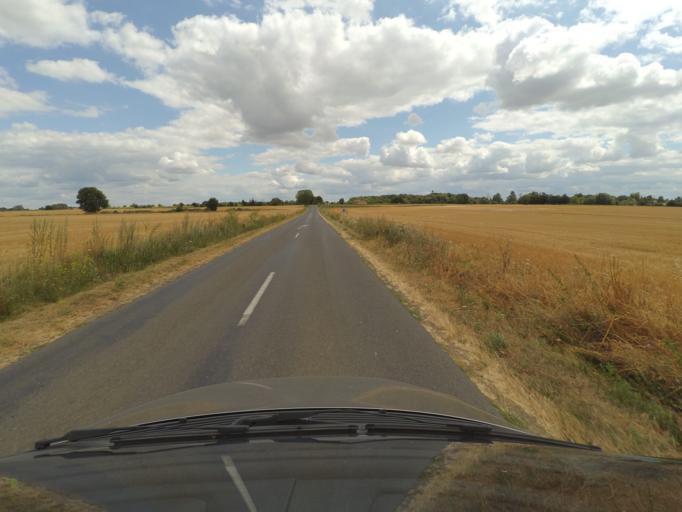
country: FR
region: Poitou-Charentes
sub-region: Departement de la Vienne
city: Saint-Savin
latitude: 46.5576
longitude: 0.9188
